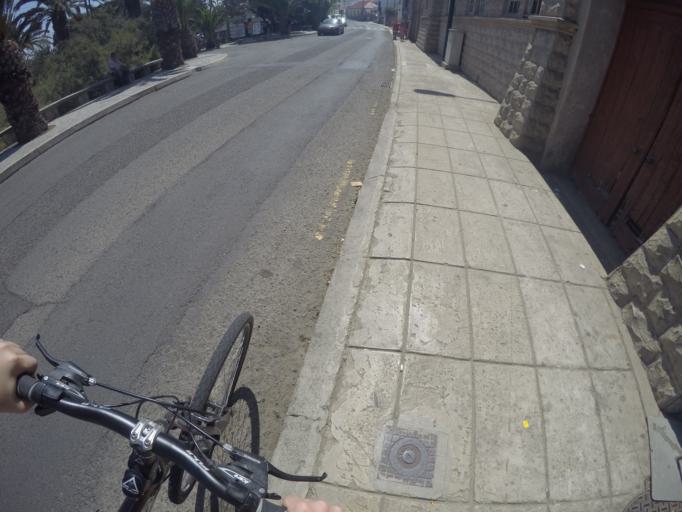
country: PT
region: Madeira
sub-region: Porto Santo
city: Vila de Porto Santo
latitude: 33.0565
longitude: -16.3380
